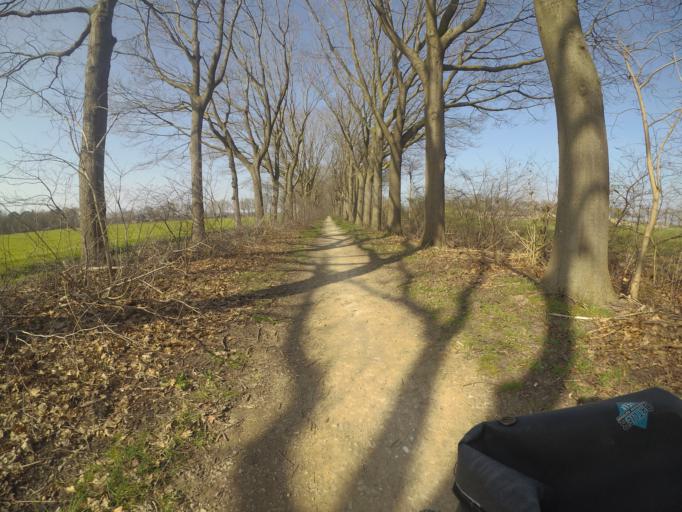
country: NL
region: North Brabant
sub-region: Gemeente Bernheze
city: Loosbroek
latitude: 51.6759
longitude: 5.4671
